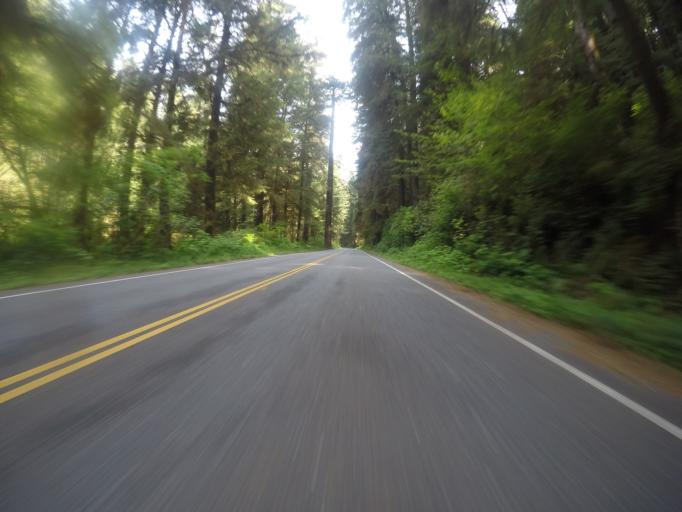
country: US
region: California
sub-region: Del Norte County
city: Bertsch-Oceanview
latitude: 41.4251
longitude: -124.0365
